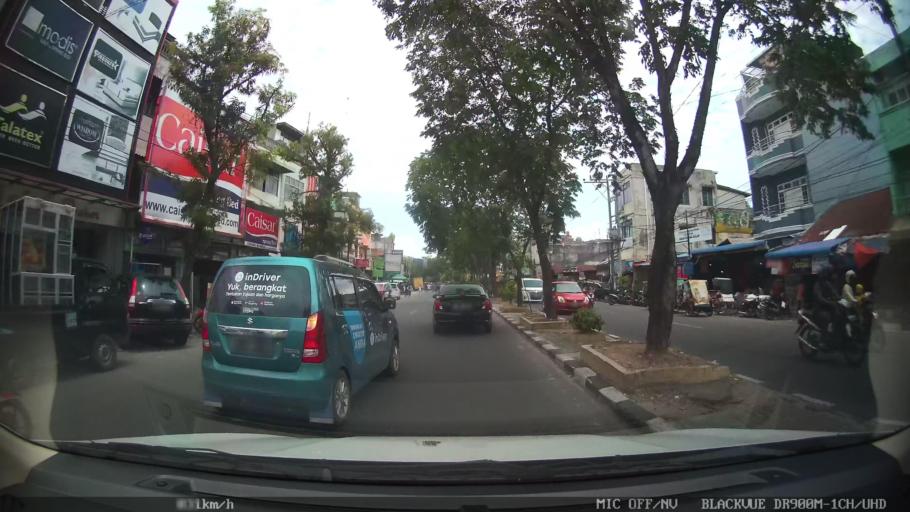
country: ID
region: North Sumatra
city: Medan
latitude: 3.5645
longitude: 98.6622
